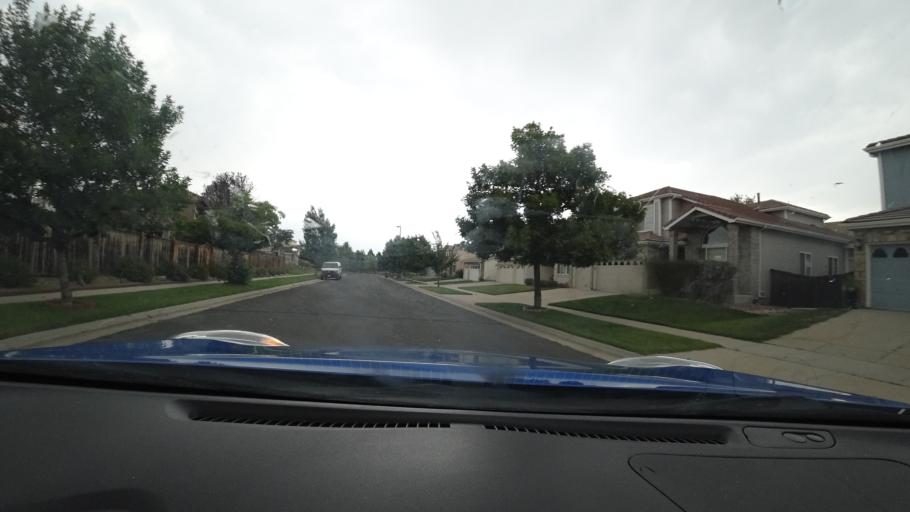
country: US
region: Colorado
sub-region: Adams County
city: Aurora
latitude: 39.7763
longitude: -104.7519
